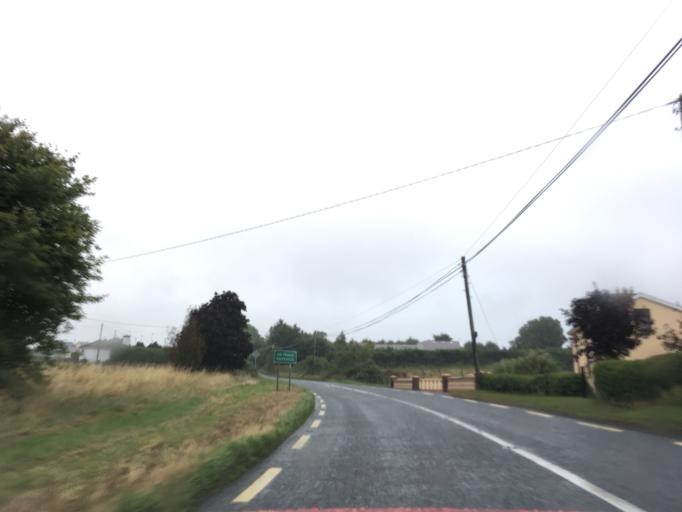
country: IE
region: Munster
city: Tipperary
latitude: 52.4847
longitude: -8.0673
